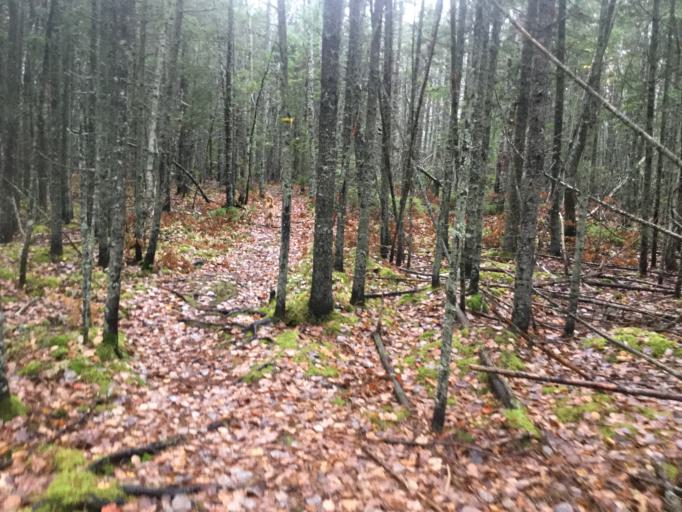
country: CA
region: Nova Scotia
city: New Glasgow
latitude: 45.5492
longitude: -62.6799
